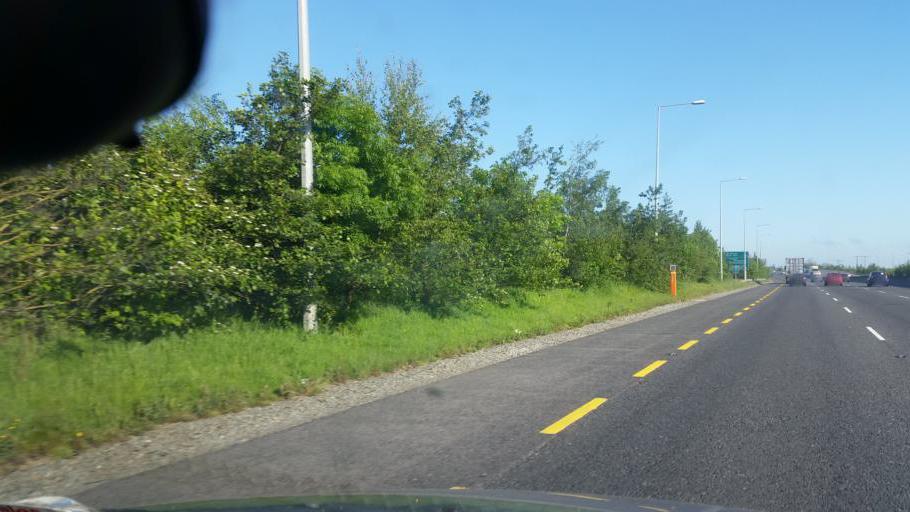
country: IE
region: Leinster
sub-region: Dublin City
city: Finglas
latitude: 53.4141
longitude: -6.3165
